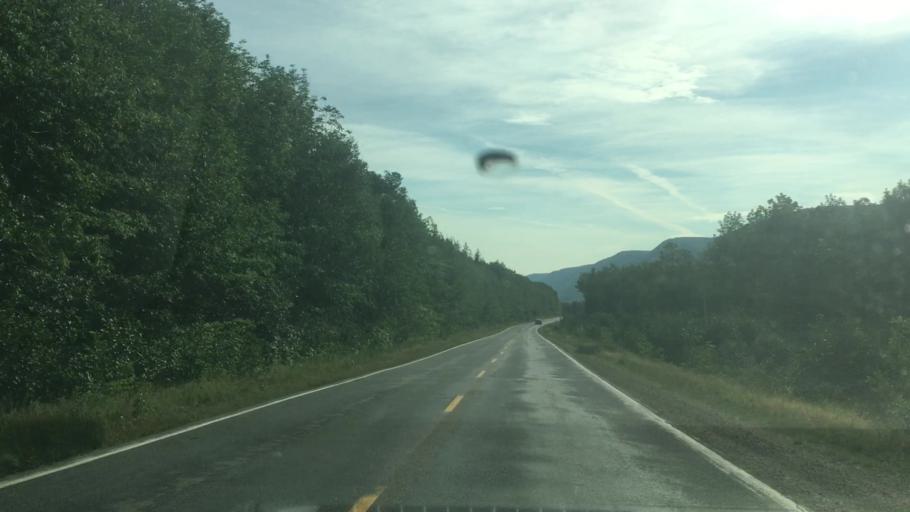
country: CA
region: Nova Scotia
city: Sydney Mines
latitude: 46.8627
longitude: -60.5645
